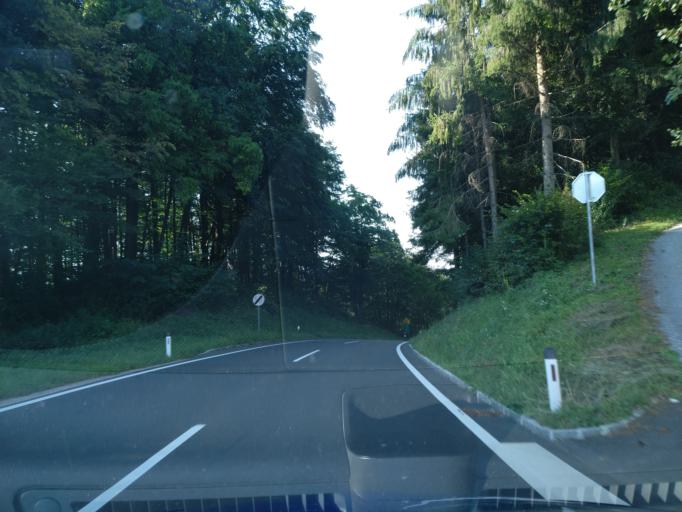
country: AT
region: Styria
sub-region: Politischer Bezirk Leibnitz
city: Gleinstatten
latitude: 46.7416
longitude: 15.3674
